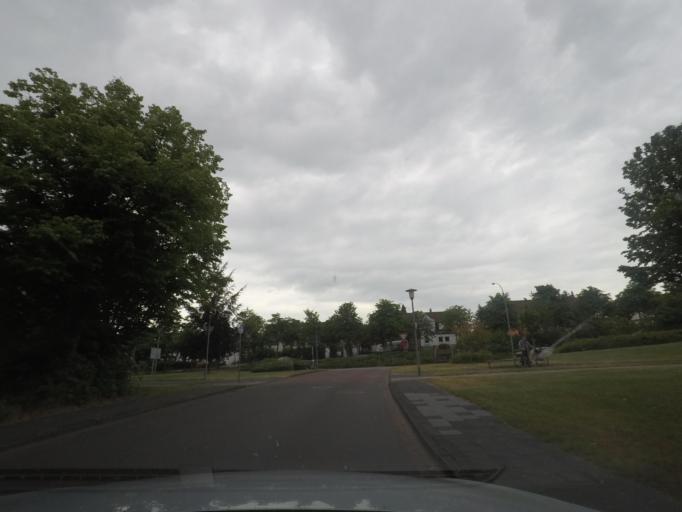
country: DE
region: Lower Saxony
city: Helmstedt
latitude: 52.2273
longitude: 11.0217
